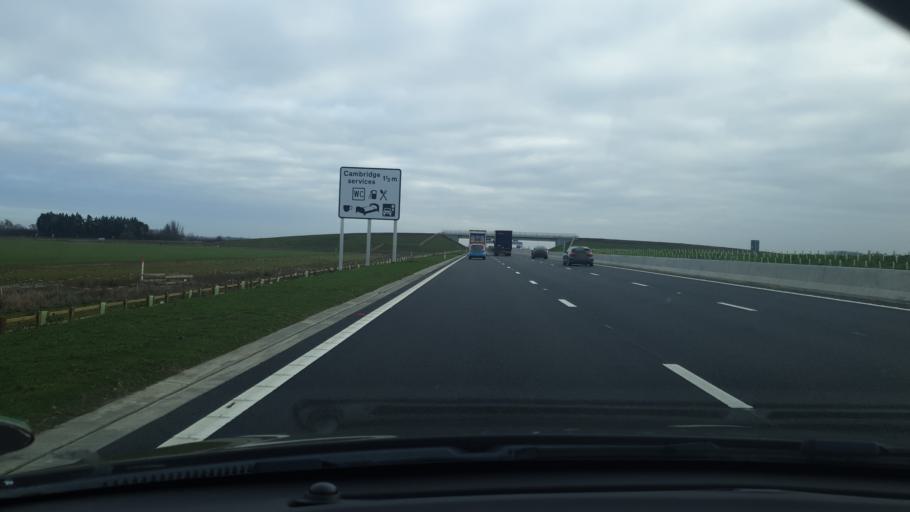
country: GB
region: England
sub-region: Cambridgeshire
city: Needingworth
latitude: 52.2870
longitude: -0.0532
